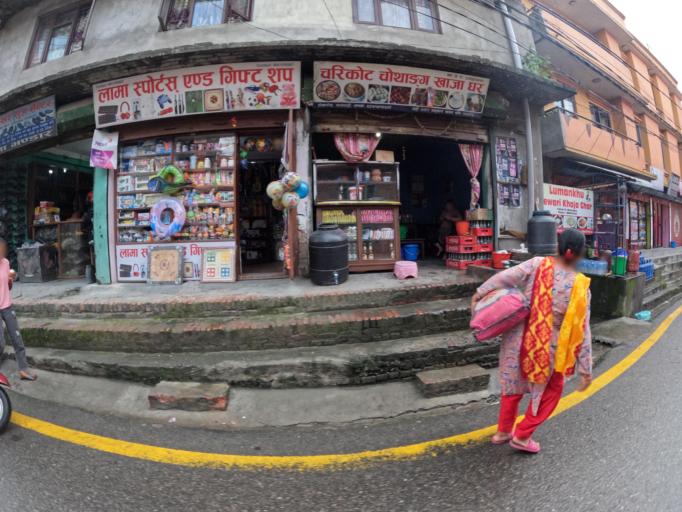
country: NP
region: Central Region
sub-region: Bagmati Zone
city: Kathmandu
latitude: 27.7377
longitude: 85.3195
